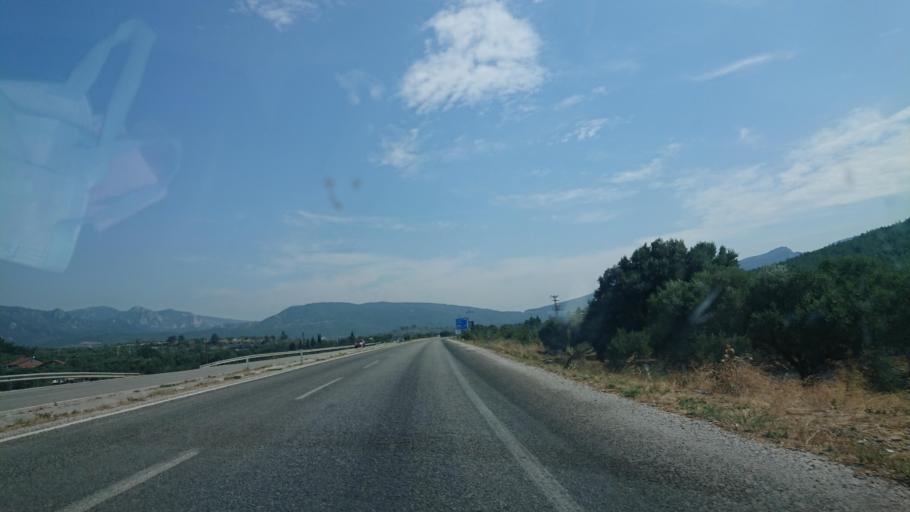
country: TR
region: Izmir
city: Dagkizilca
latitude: 38.3055
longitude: 27.4097
